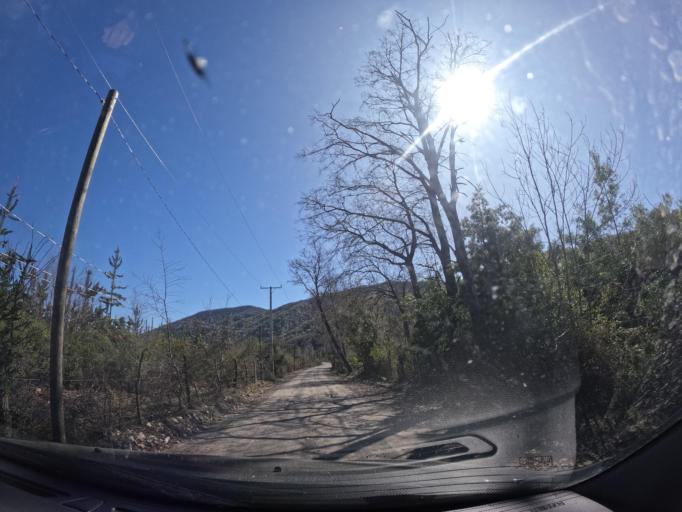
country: CL
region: Maule
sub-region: Provincia de Linares
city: Longavi
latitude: -36.2302
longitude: -71.3734
